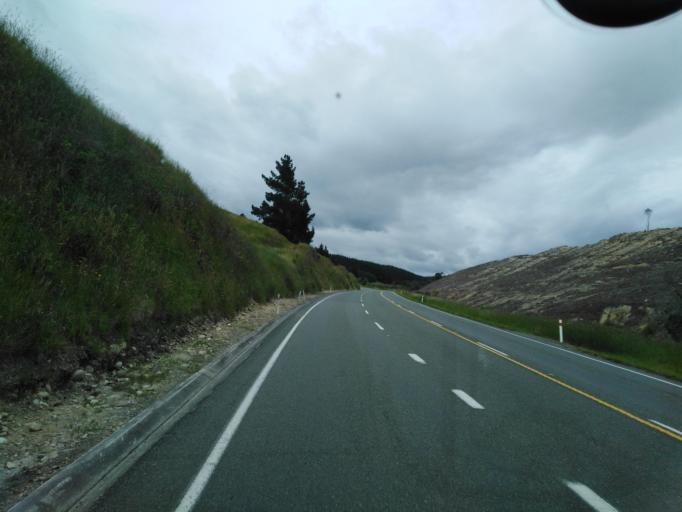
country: NZ
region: Tasman
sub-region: Tasman District
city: Wakefield
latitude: -41.4655
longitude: 172.9466
